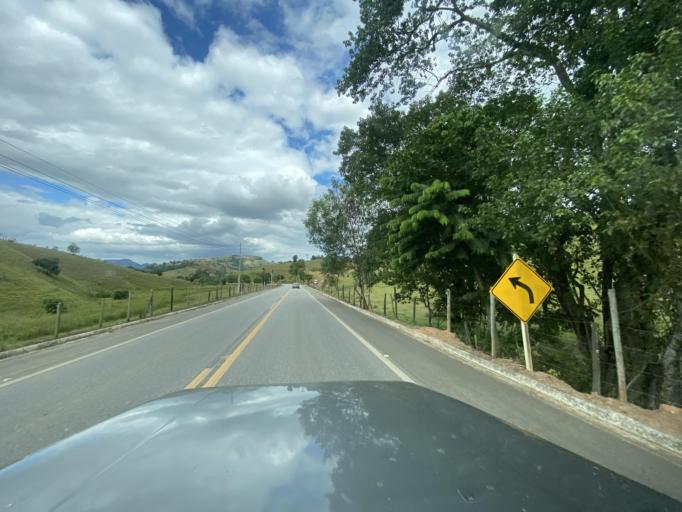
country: BR
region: Espirito Santo
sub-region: Jeronimo Monteiro
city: Jeronimo Monteiro
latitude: -20.7776
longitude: -41.4191
